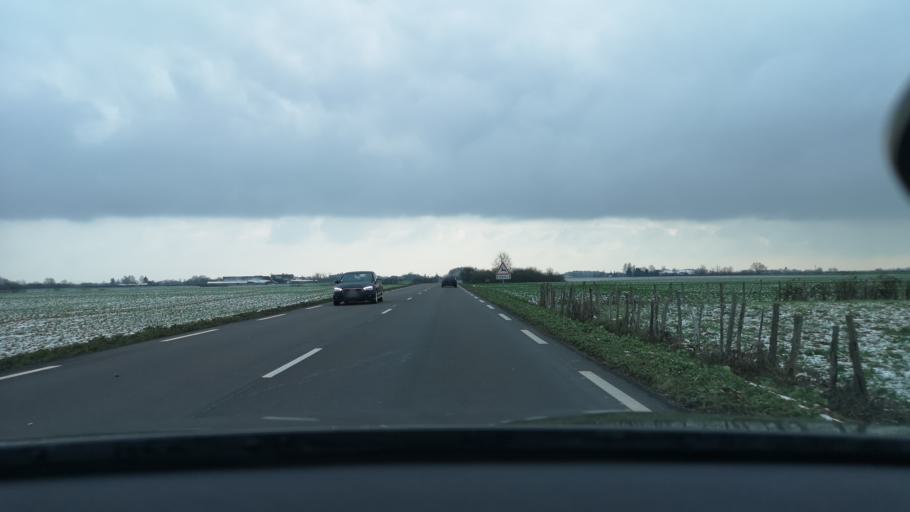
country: FR
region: Bourgogne
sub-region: Departement de Saone-et-Loire
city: Saint-Martin-en-Bresse
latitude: 46.7460
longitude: 5.0580
